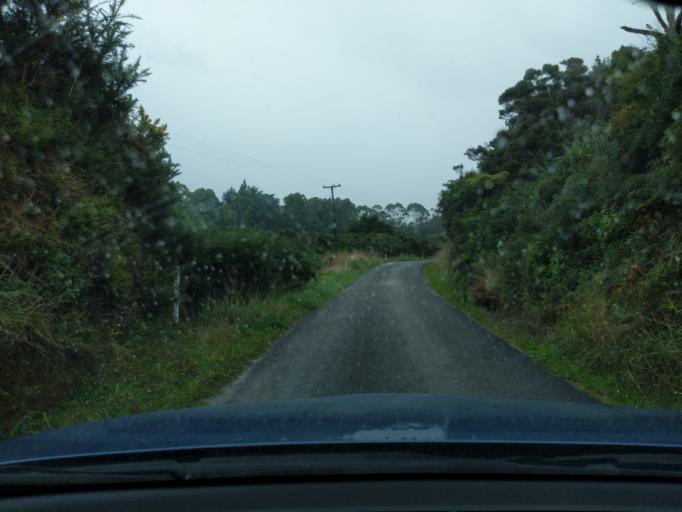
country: NZ
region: Tasman
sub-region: Tasman District
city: Takaka
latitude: -40.6362
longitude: 172.4893
